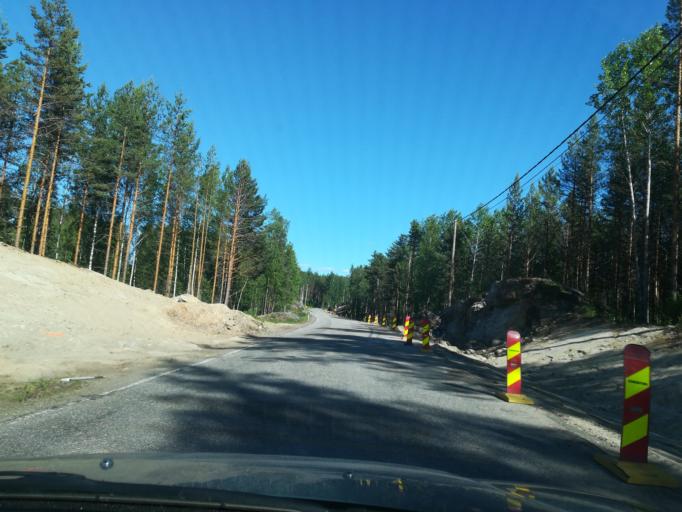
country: FI
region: Southern Savonia
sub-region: Mikkeli
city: Puumala
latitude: 61.4681
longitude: 28.3193
